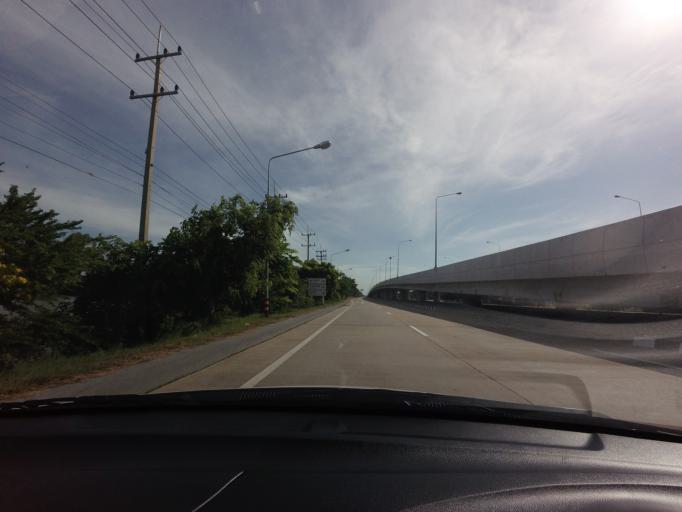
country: TH
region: Suphan Buri
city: Suphan Buri
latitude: 14.4974
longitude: 100.0470
